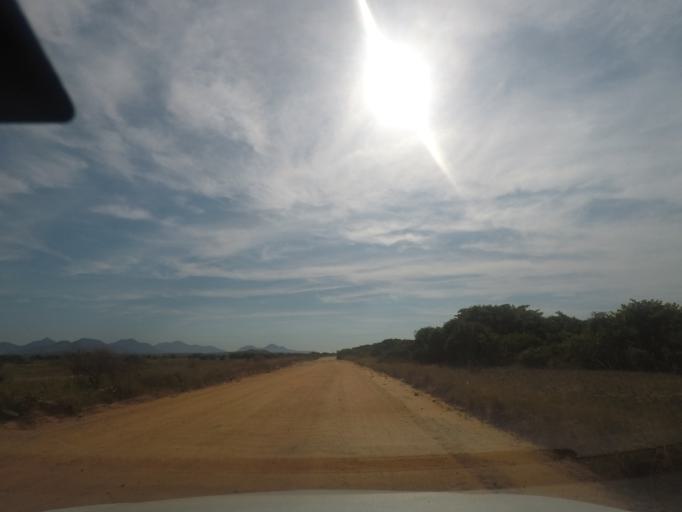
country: BR
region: Rio de Janeiro
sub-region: Marica
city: Marica
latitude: -22.9605
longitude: -42.8526
